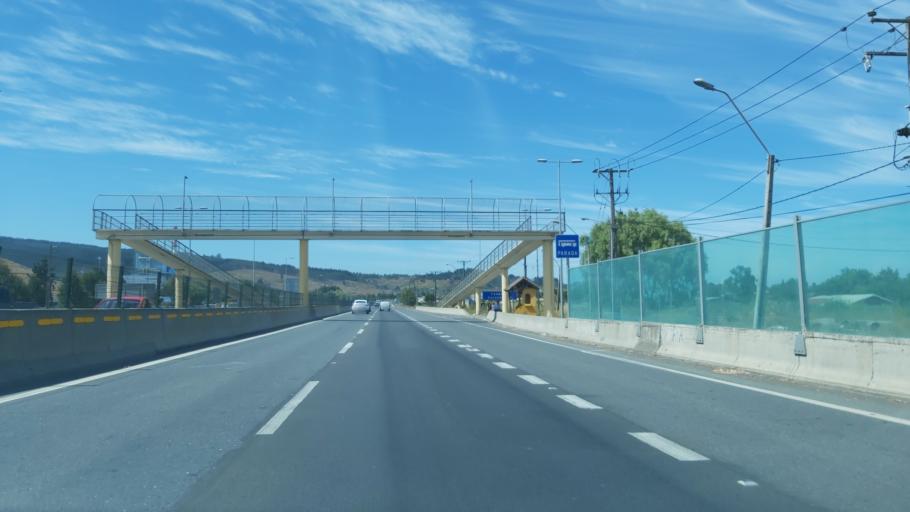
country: CL
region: Biobio
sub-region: Provincia de Concepcion
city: Coronel
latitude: -37.0318
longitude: -73.1350
